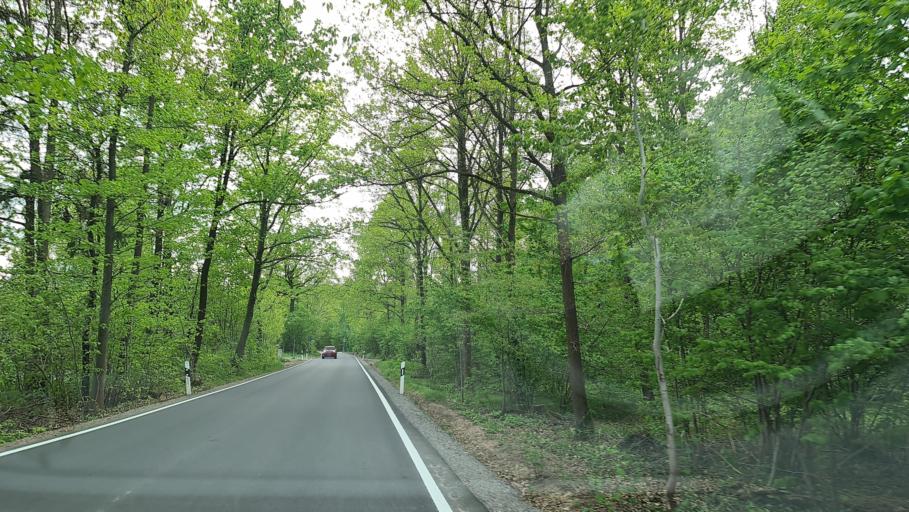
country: DE
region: Saxony
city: Hilbersdorf
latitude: 50.8399
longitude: 12.9885
